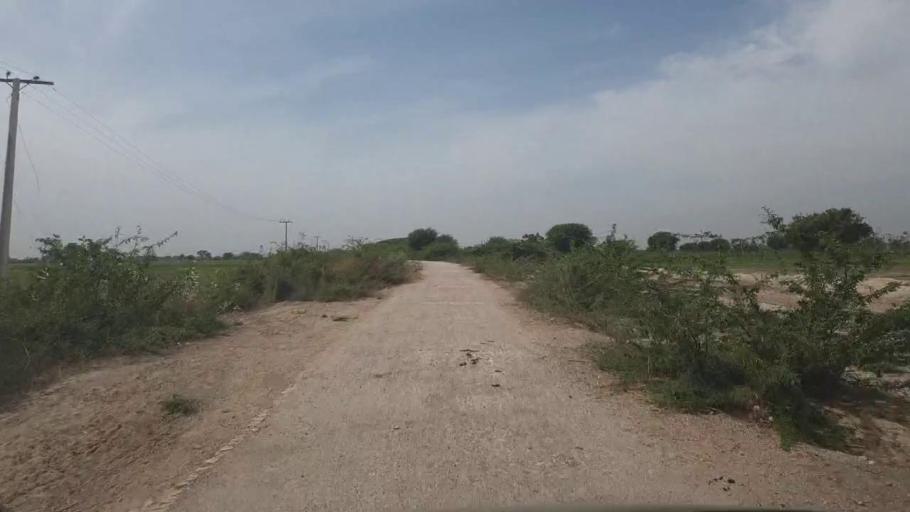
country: PK
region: Sindh
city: Umarkot
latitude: 25.2197
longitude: 69.7087
